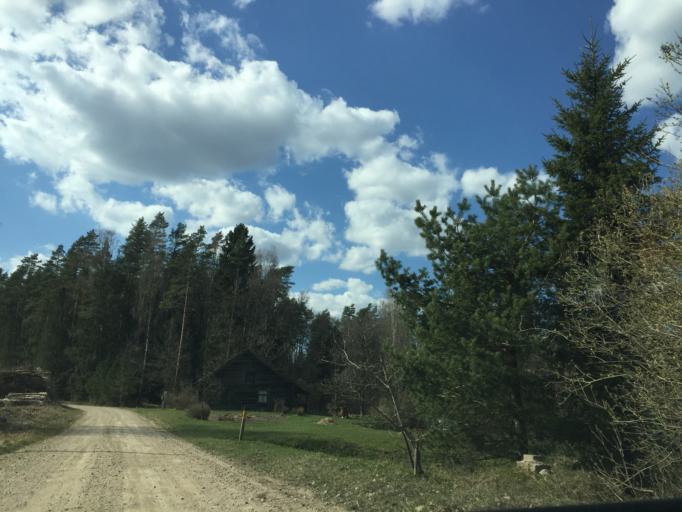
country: LV
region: Skriveri
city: Skriveri
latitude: 56.7848
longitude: 25.2158
